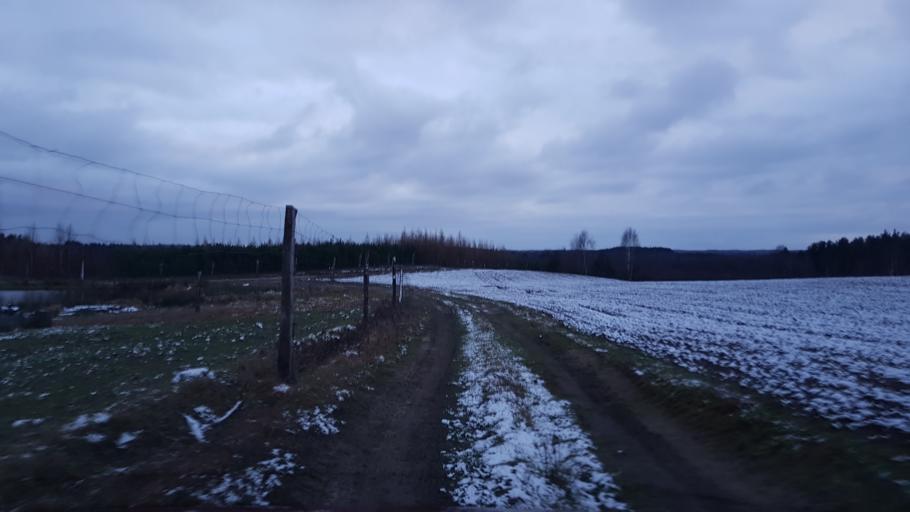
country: PL
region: Pomeranian Voivodeship
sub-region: Powiat bytowski
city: Tuchomie
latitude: 54.1480
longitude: 17.3031
